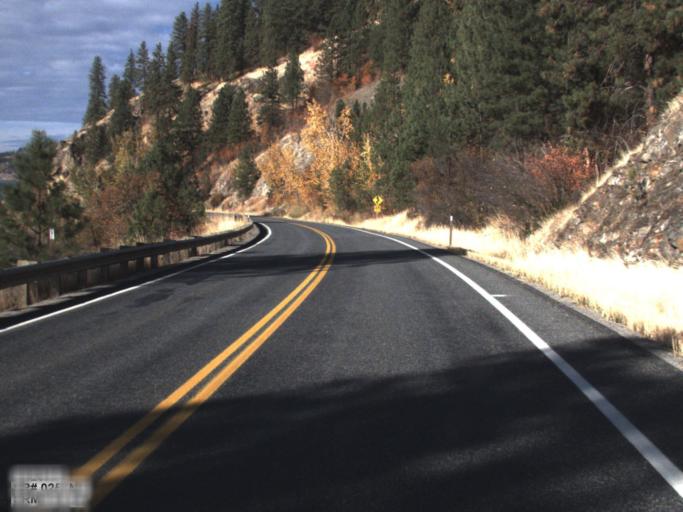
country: US
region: Washington
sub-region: Stevens County
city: Kettle Falls
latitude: 48.6355
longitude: -118.0810
